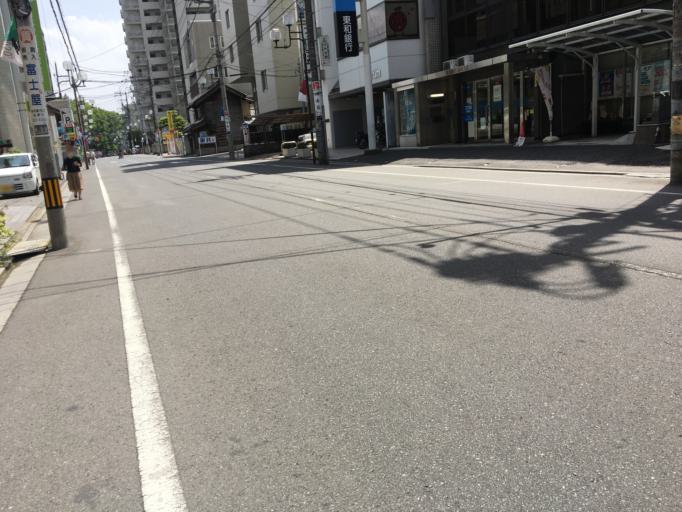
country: JP
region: Saitama
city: Yono
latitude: 35.8557
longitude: 139.6545
